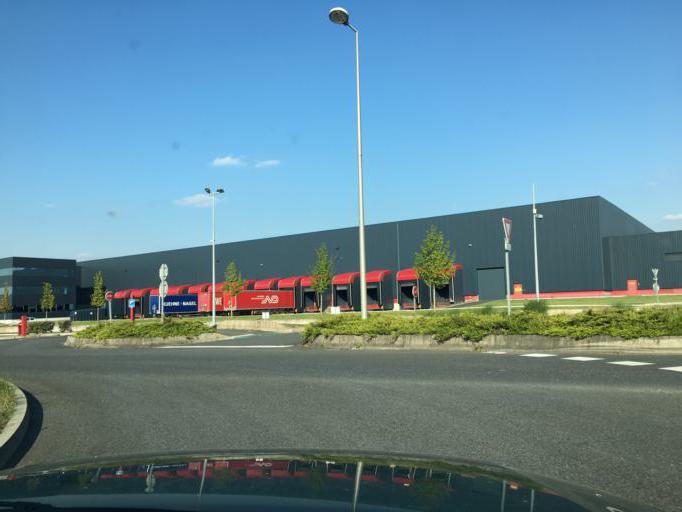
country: FR
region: Centre
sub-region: Departement du Loiret
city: Gidy
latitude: 47.9594
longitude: 1.8461
